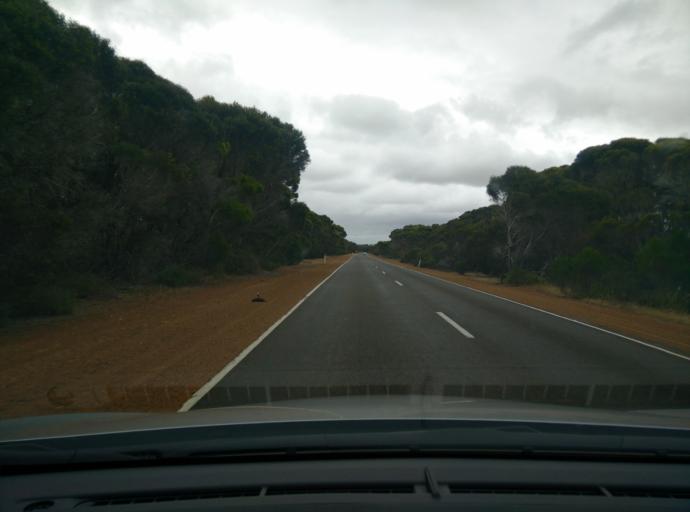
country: AU
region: South Australia
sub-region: Kangaroo Island
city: Kingscote
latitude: -35.7123
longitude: 137.5630
